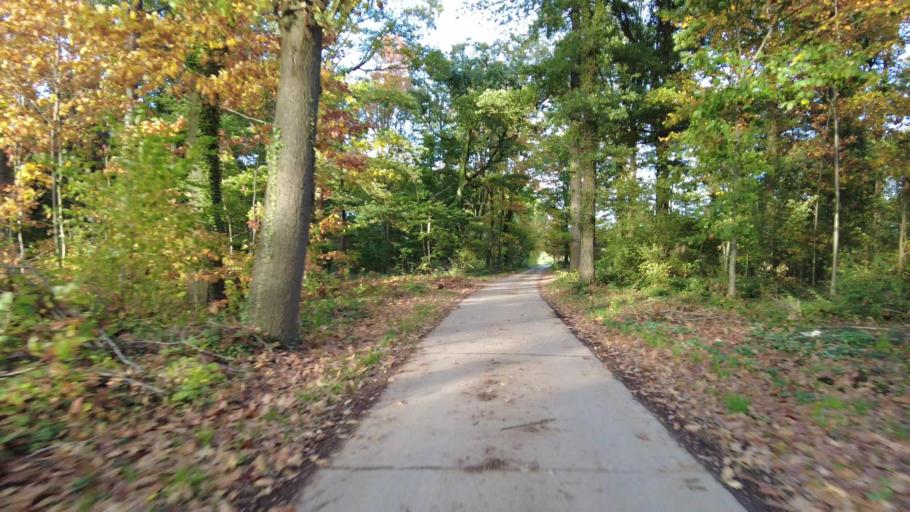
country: BE
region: Flanders
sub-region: Provincie Vlaams-Brabant
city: Hoegaarden
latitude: 50.7348
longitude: 4.9478
